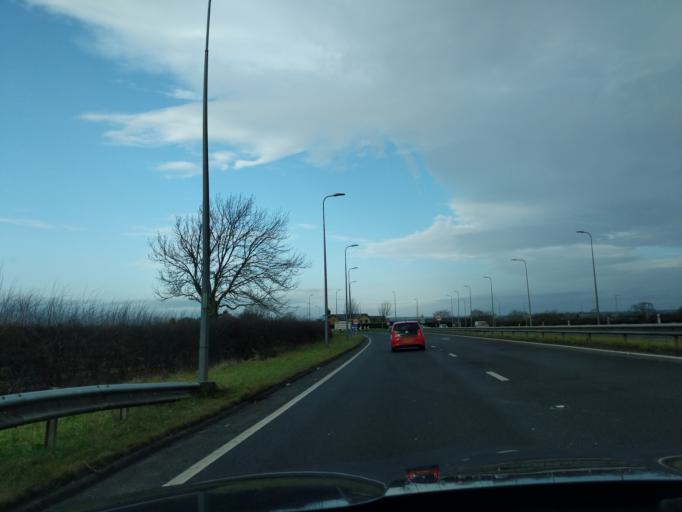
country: GB
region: England
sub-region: Northumberland
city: Ponteland
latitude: 55.0383
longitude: -1.7161
